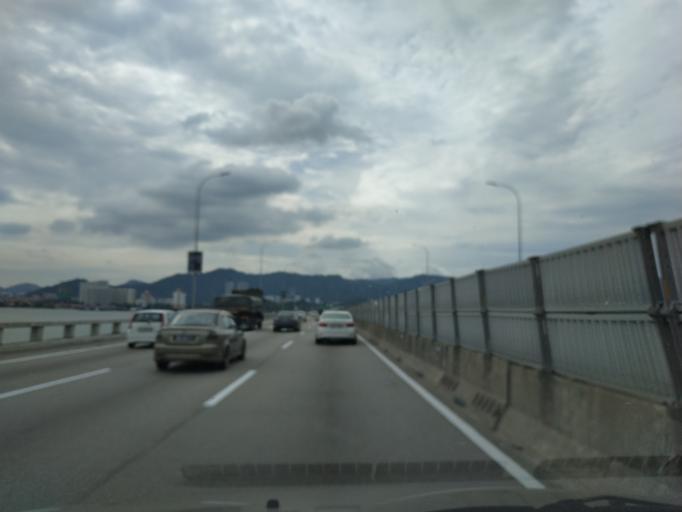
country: MY
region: Penang
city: George Town
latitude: 5.3568
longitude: 100.3286
